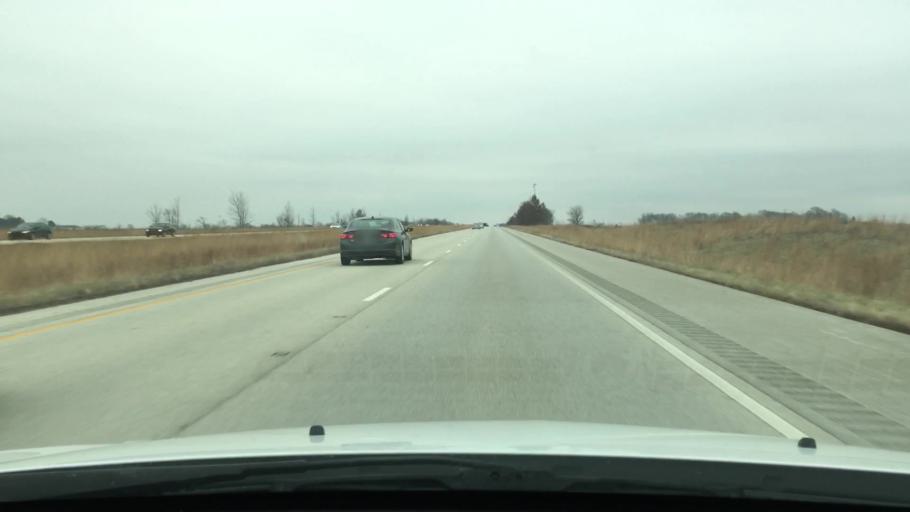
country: US
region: Illinois
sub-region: Sangamon County
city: New Berlin
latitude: 39.7404
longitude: -89.8855
